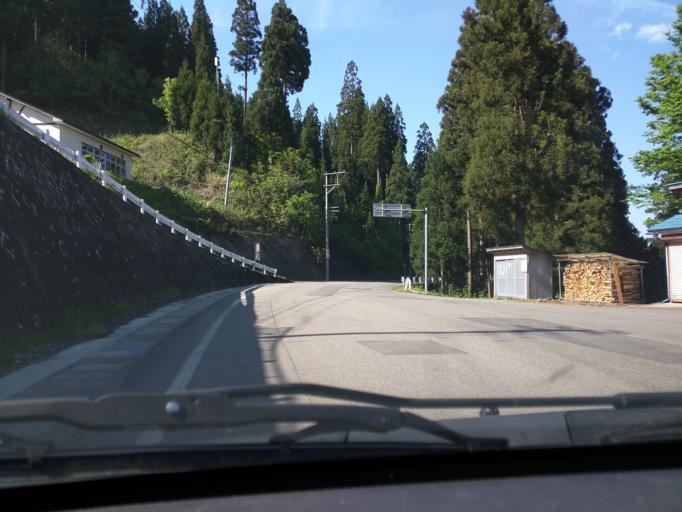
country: JP
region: Fukushima
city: Kitakata
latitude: 37.5573
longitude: 139.6246
